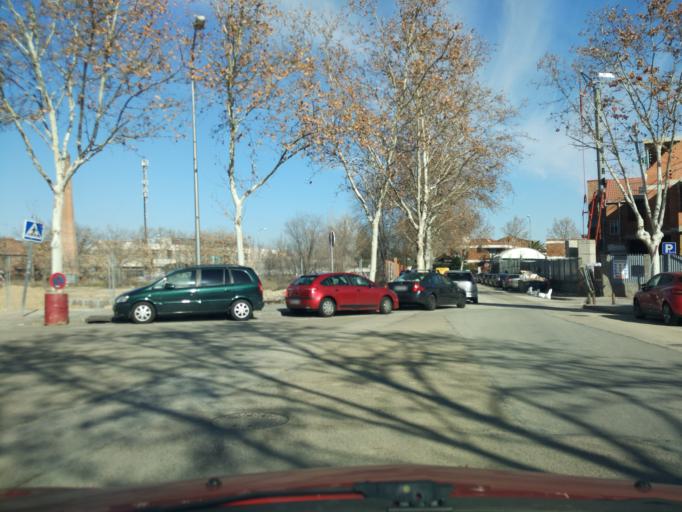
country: ES
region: Madrid
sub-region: Provincia de Madrid
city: San Blas
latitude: 40.4415
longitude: -3.6171
